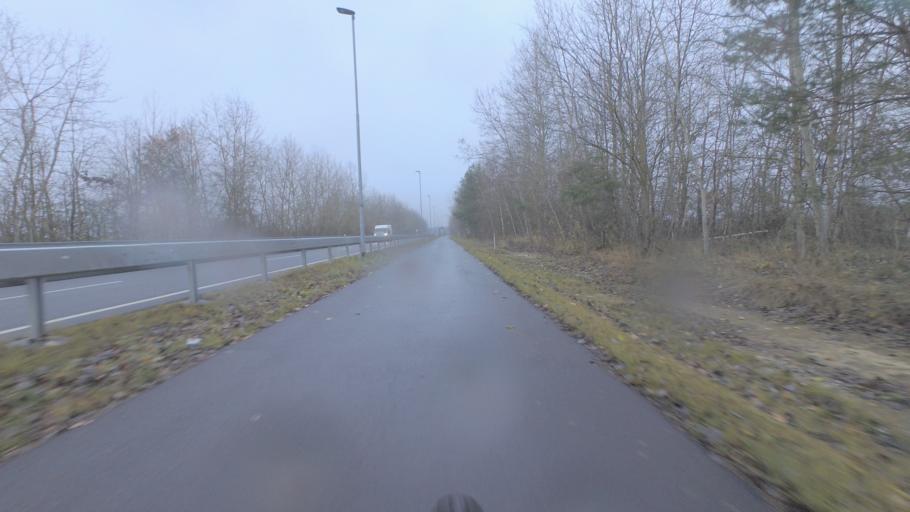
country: DE
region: Brandenburg
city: Ludwigsfelde
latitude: 52.3209
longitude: 13.2833
